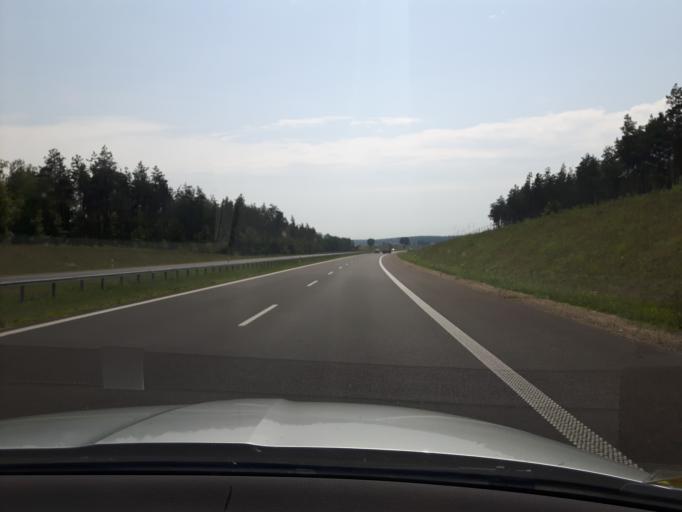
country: PL
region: Masovian Voivodeship
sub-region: Powiat mlawski
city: Wieczfnia Koscielna
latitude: 53.2408
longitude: 20.4238
